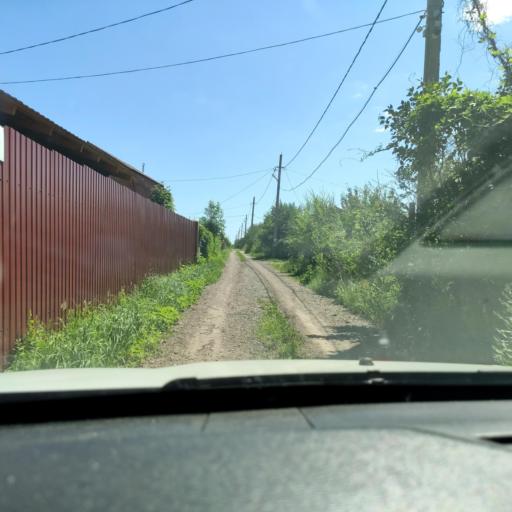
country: RU
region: Samara
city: Dubovyy Umet
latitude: 53.0313
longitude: 50.2486
